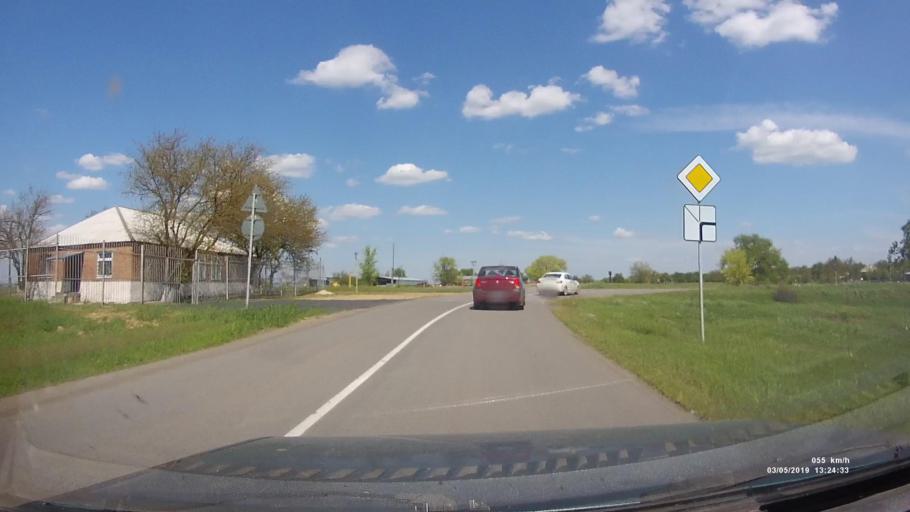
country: RU
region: Rostov
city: Semikarakorsk
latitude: 47.5662
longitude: 40.7970
